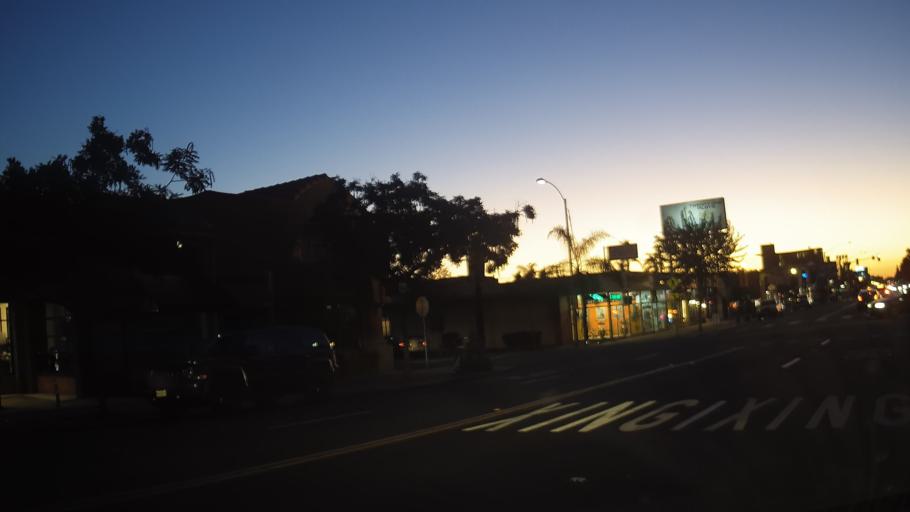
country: US
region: California
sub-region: San Diego County
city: San Diego
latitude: 32.7485
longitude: -117.1479
